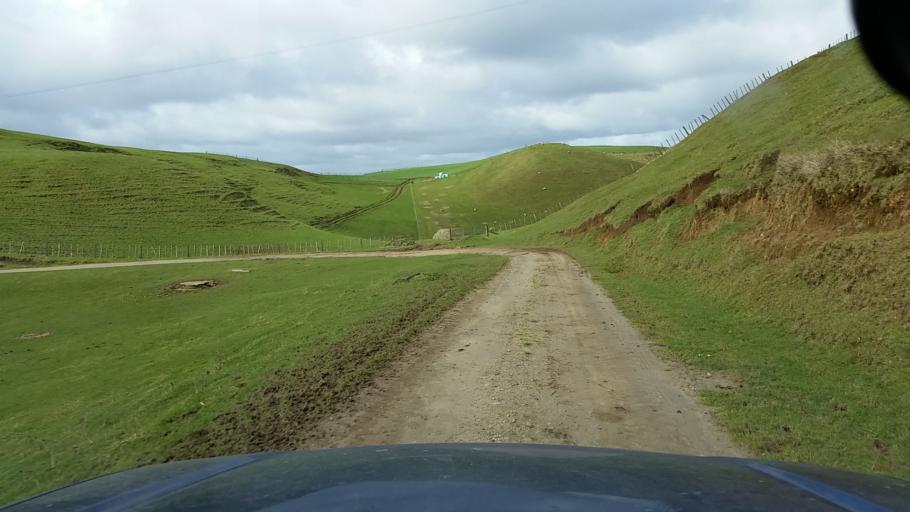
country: NZ
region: Taranaki
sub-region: South Taranaki District
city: Patea
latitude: -39.6601
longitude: 174.5684
